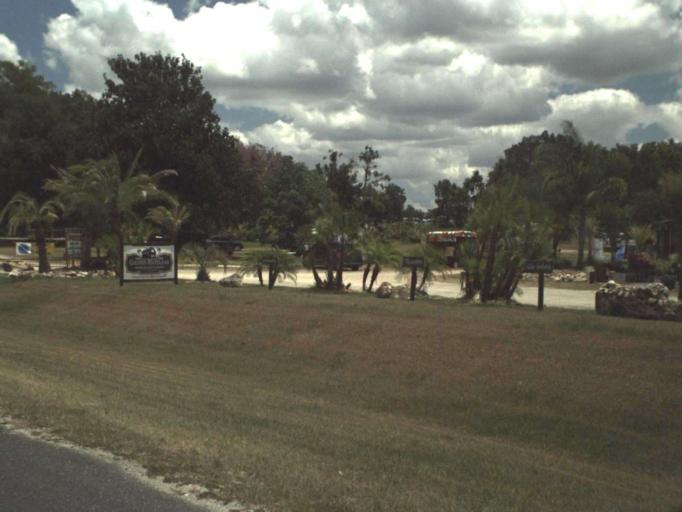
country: US
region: Florida
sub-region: Sumter County
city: Wildwood
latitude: 28.9163
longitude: -82.0369
